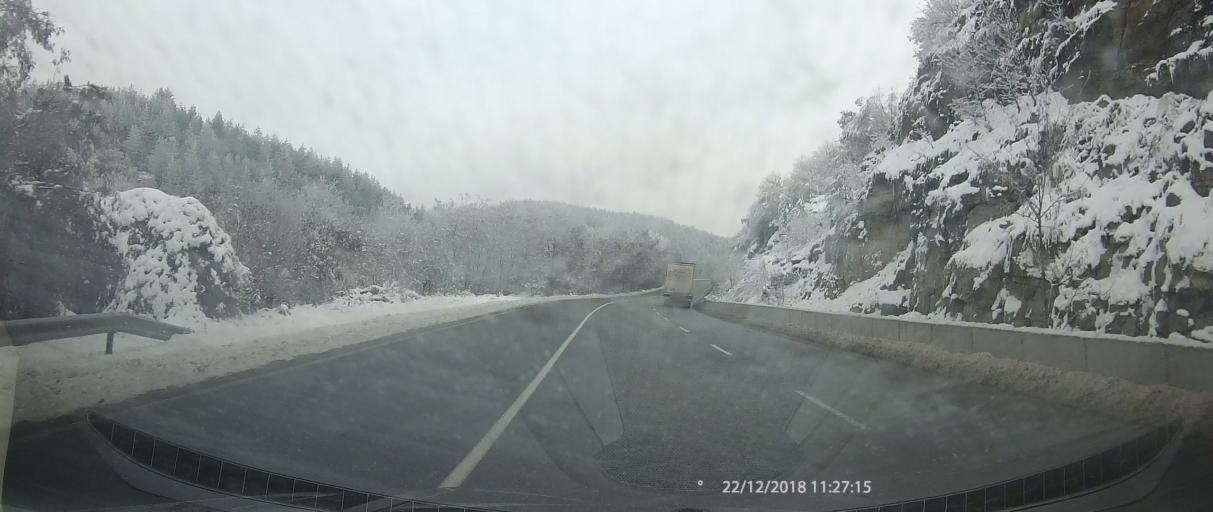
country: BG
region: Kyustendil
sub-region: Obshtina Bobovdol
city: Bobovdol
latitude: 42.2741
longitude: 22.9315
